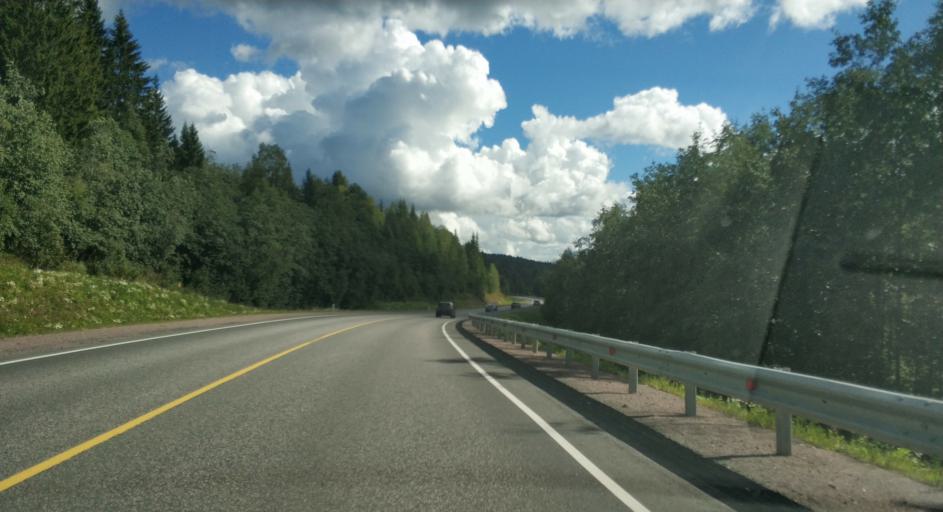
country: RU
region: Republic of Karelia
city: Ruskeala
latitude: 61.9216
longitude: 30.6118
